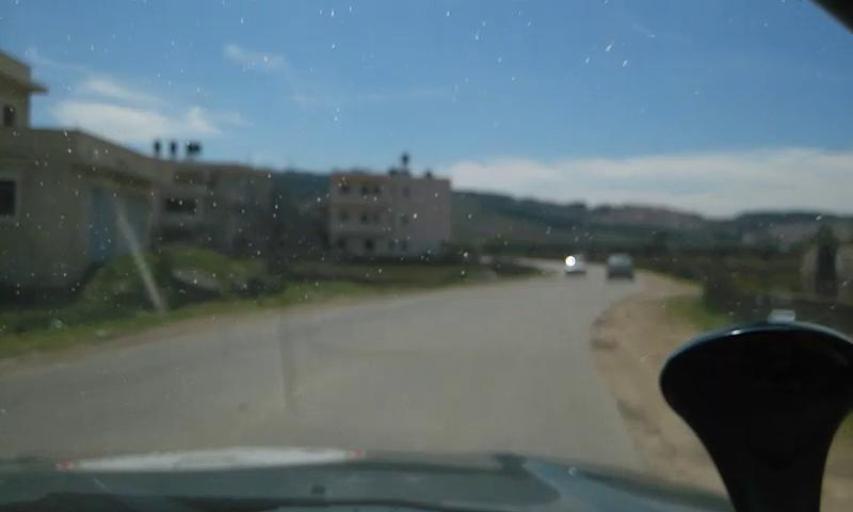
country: PS
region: West Bank
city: Al Jib
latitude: 31.8502
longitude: 35.1807
